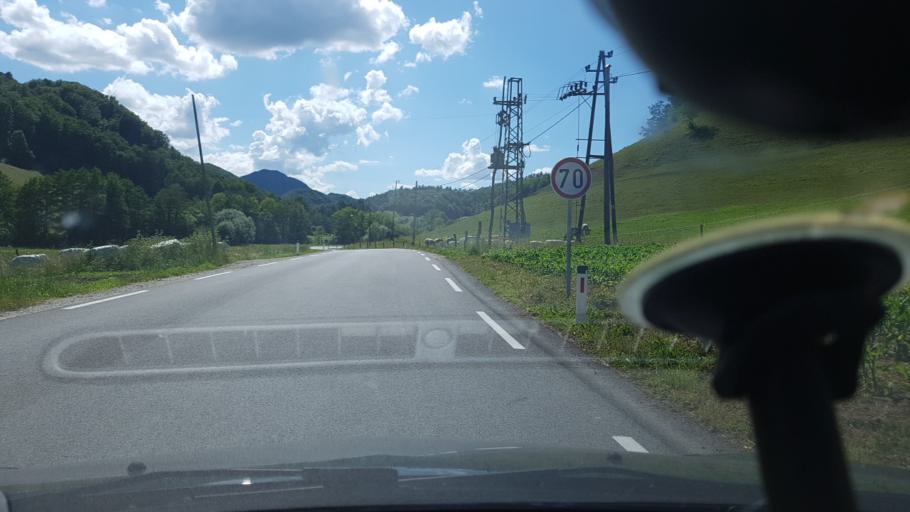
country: SI
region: Zetale
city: Zetale
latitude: 46.2884
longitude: 15.8342
